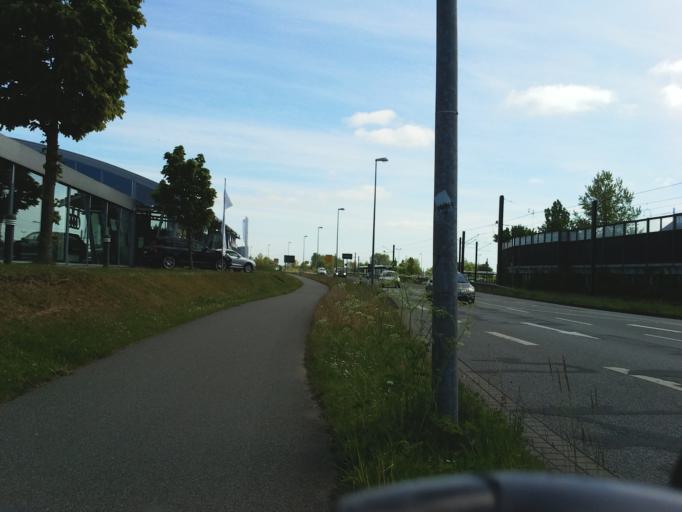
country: DE
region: Mecklenburg-Vorpommern
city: Papendorf
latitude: 54.0595
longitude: 12.1175
